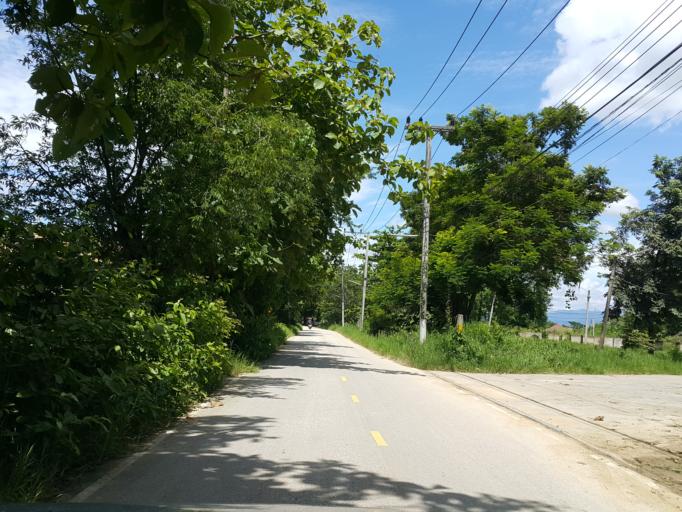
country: TH
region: Chiang Mai
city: San Kamphaeng
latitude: 18.7649
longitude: 99.0983
